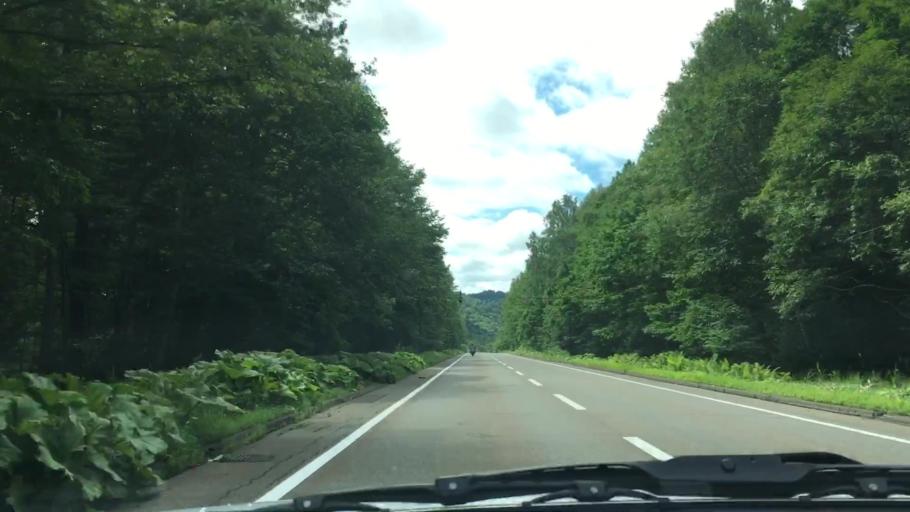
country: JP
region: Hokkaido
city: Kitami
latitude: 43.3980
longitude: 143.9258
